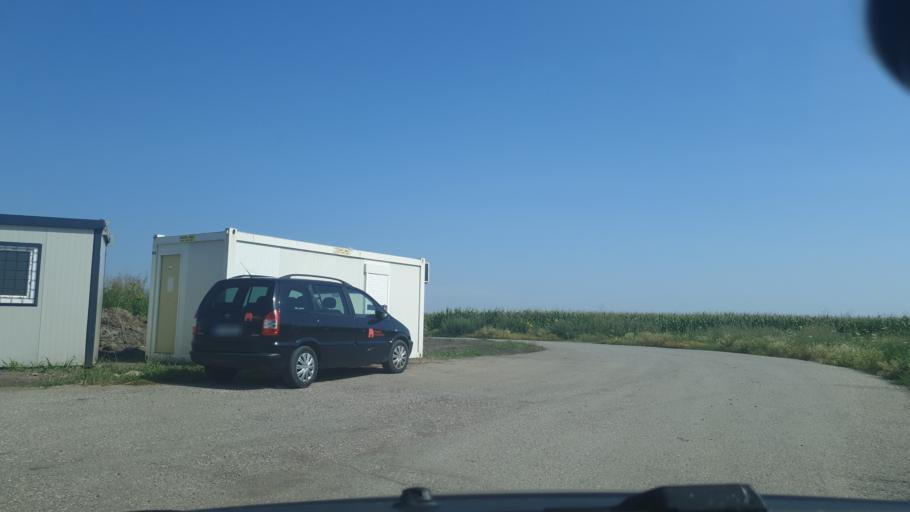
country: RS
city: Simanovci
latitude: 44.8965
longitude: 20.0990
